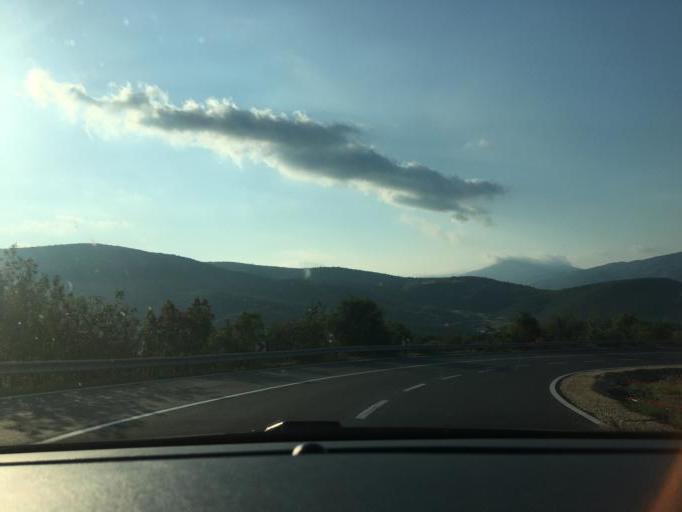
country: MK
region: Valandovo
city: Valandovo
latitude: 41.3240
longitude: 22.5973
